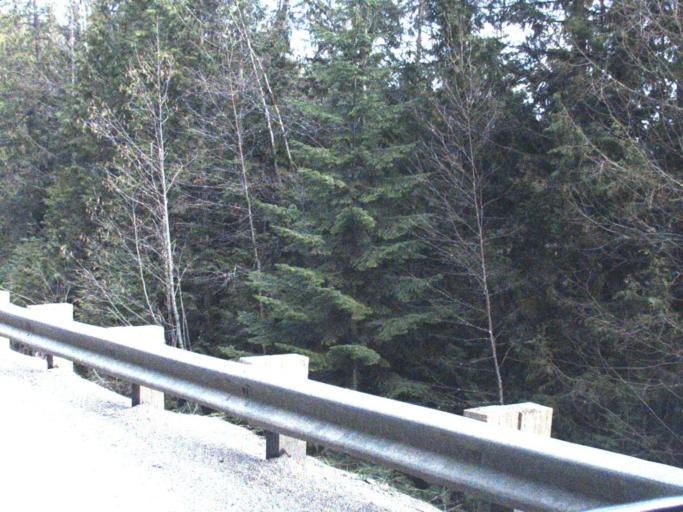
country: US
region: Washington
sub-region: Stevens County
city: Chewelah
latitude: 48.5649
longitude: -117.3526
